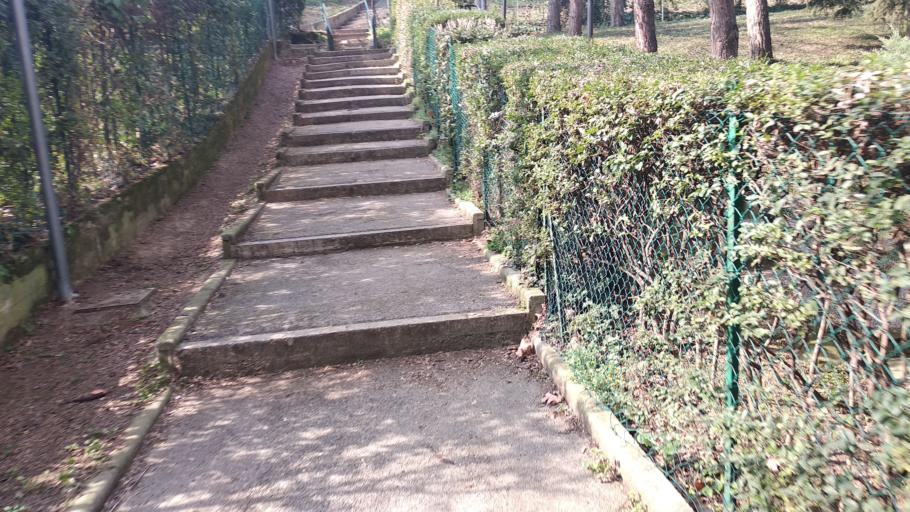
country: IT
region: Emilia-Romagna
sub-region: Provincia di Bologna
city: Ponticella
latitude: 44.4585
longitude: 11.3726
